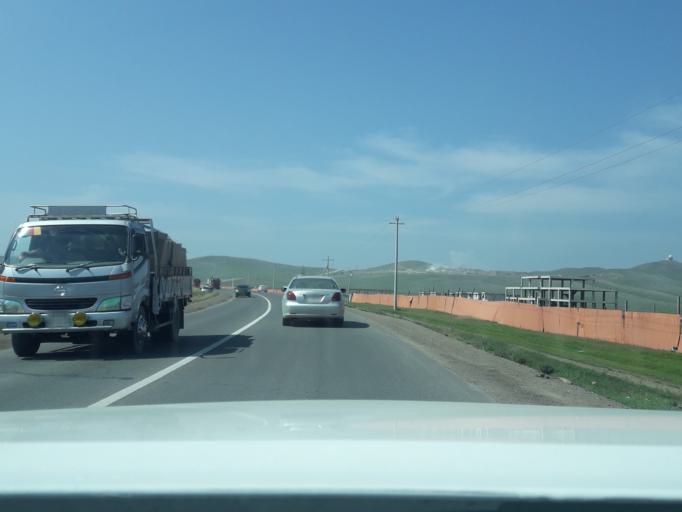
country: MN
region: Ulaanbaatar
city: Ulaanbaatar
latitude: 47.8259
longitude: 106.7700
